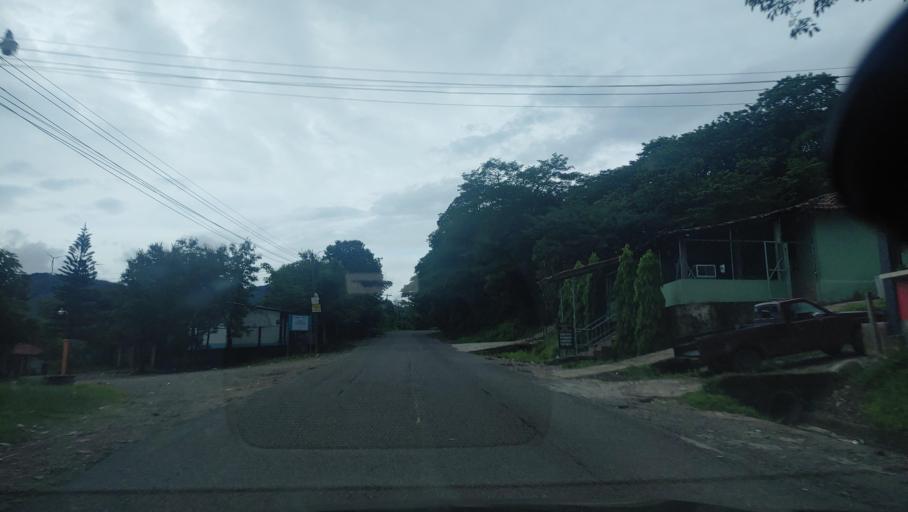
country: HN
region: Choluteca
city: Corpus
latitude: 13.3714
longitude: -86.9991
